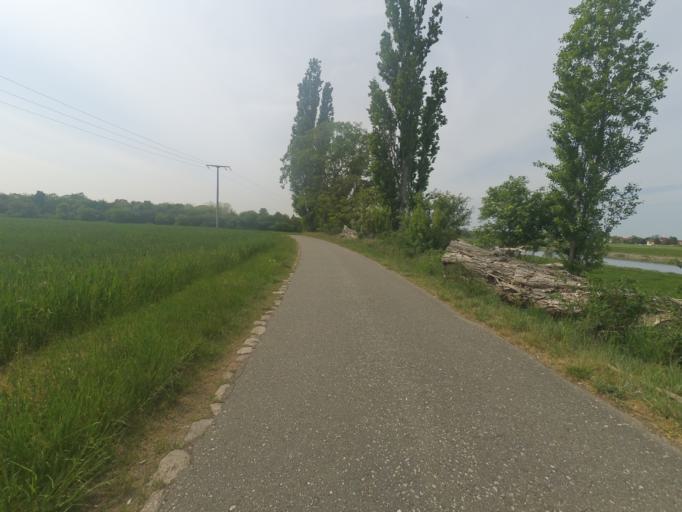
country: DE
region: Saxony
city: Strehla
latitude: 51.3470
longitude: 13.2536
